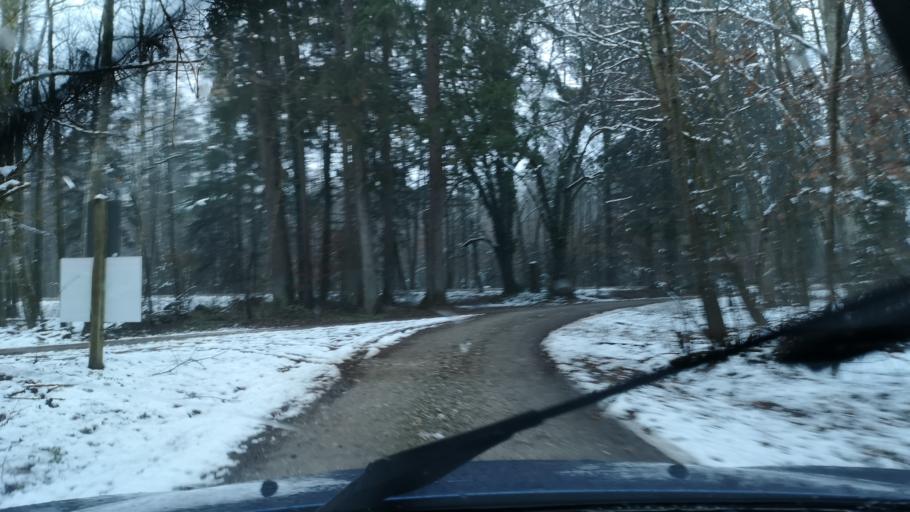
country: DE
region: Bavaria
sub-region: Upper Bavaria
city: Anzing
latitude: 48.1382
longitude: 11.8709
